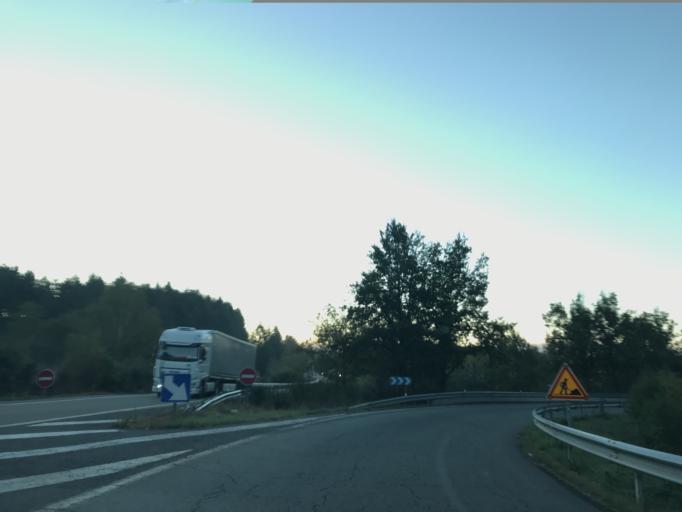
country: FR
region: Auvergne
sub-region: Departement du Puy-de-Dome
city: Celles-sur-Durolle
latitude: 45.8826
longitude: 3.6243
